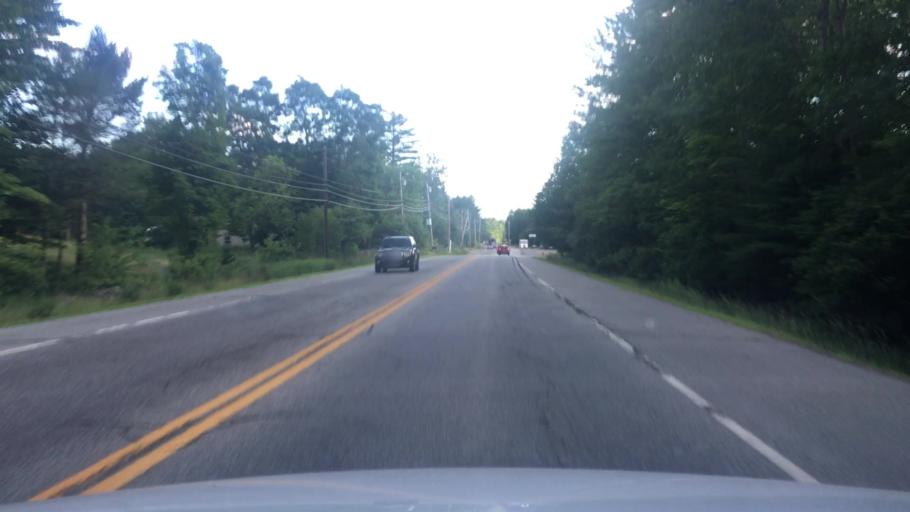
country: US
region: Maine
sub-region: Franklin County
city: Wilton
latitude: 44.5701
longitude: -70.2303
